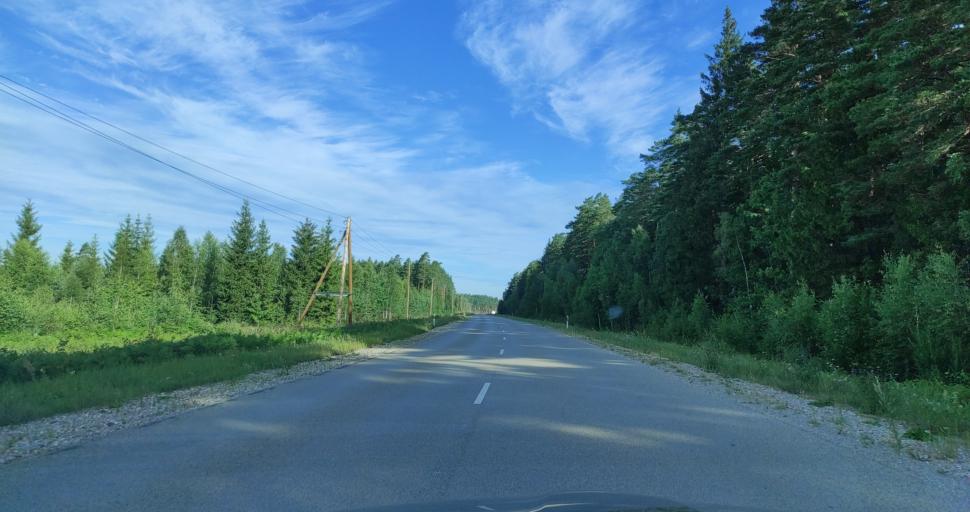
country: LV
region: Pavilostas
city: Pavilosta
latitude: 56.7914
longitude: 21.2445
